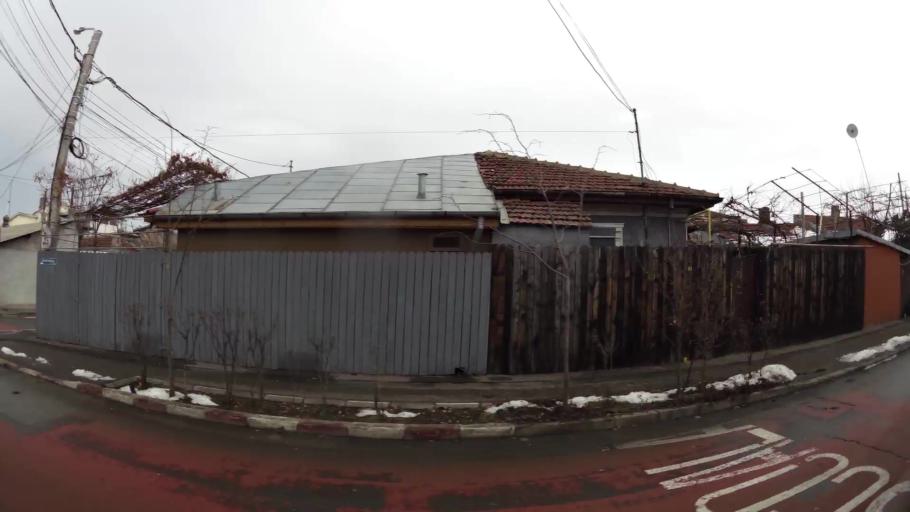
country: RO
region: Ilfov
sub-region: Comuna Pantelimon
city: Pantelimon
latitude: 44.4346
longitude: 26.1964
